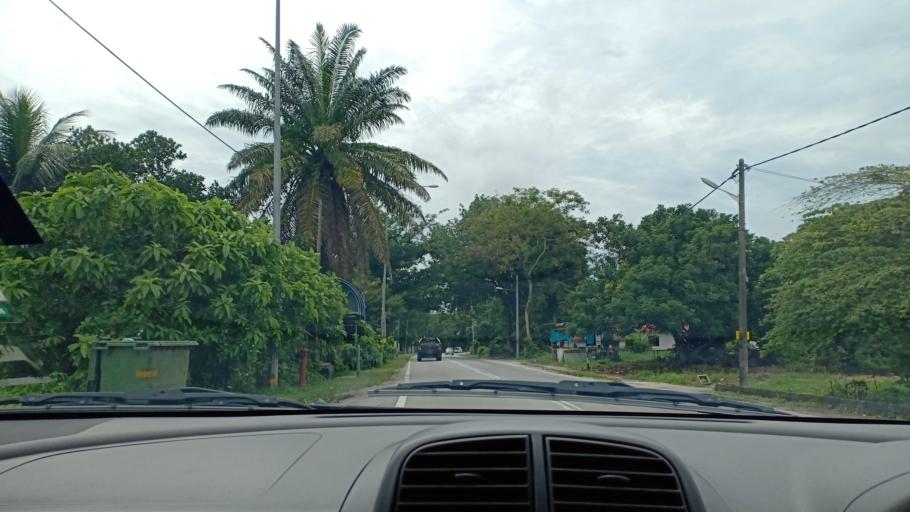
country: MY
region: Penang
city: Bukit Mertajam
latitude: 5.4084
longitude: 100.4814
